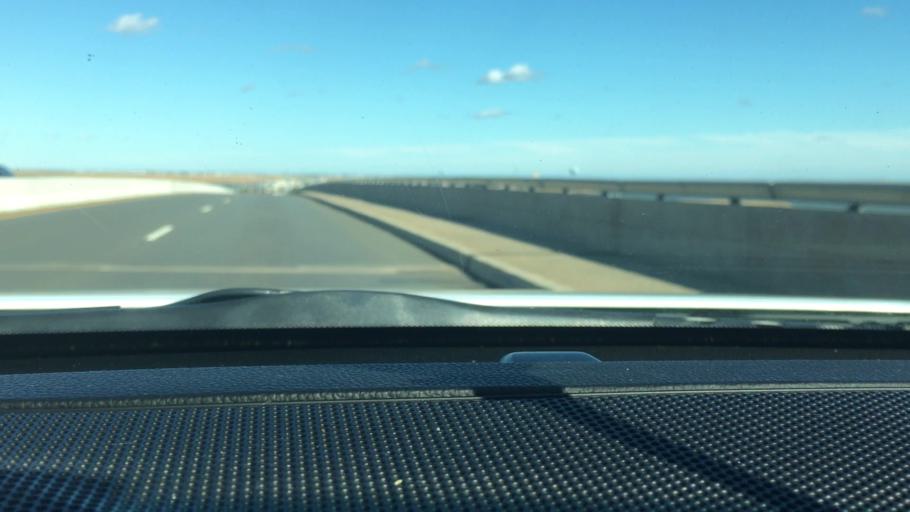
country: US
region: New Jersey
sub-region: Atlantic County
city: Atlantic City
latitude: 39.3855
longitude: -74.4209
